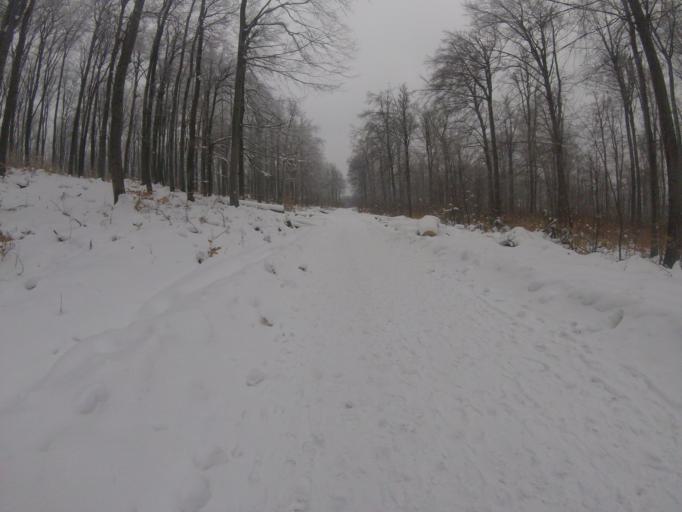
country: HU
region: Pest
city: Pilisszanto
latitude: 47.6986
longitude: 18.8602
